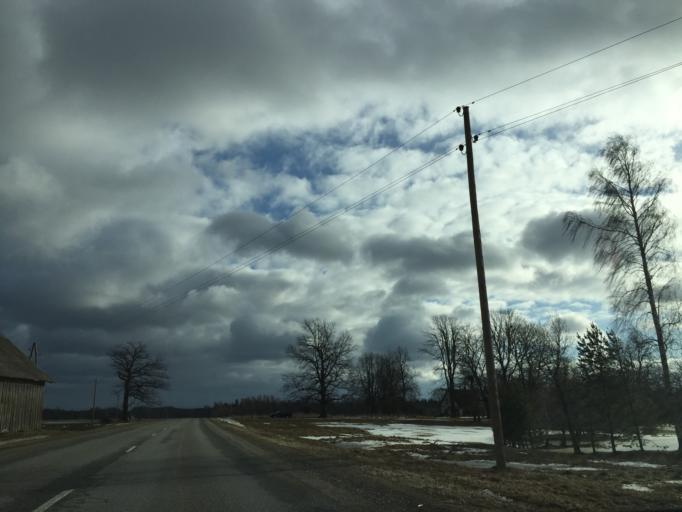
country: LV
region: Aloja
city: Staicele
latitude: 57.8724
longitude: 24.6802
